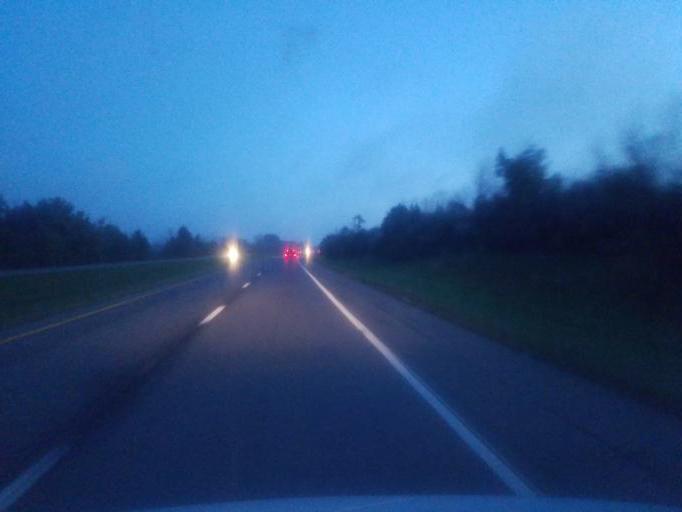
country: US
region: Ohio
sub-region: Trumbull County
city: Cortland
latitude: 41.4171
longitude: -80.7101
